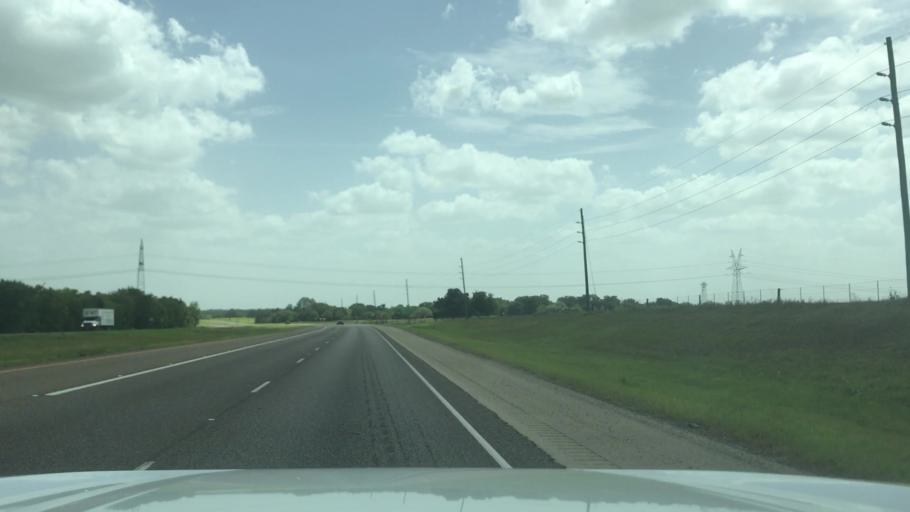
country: US
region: Texas
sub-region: Robertson County
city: Calvert
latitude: 31.1015
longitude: -96.7149
